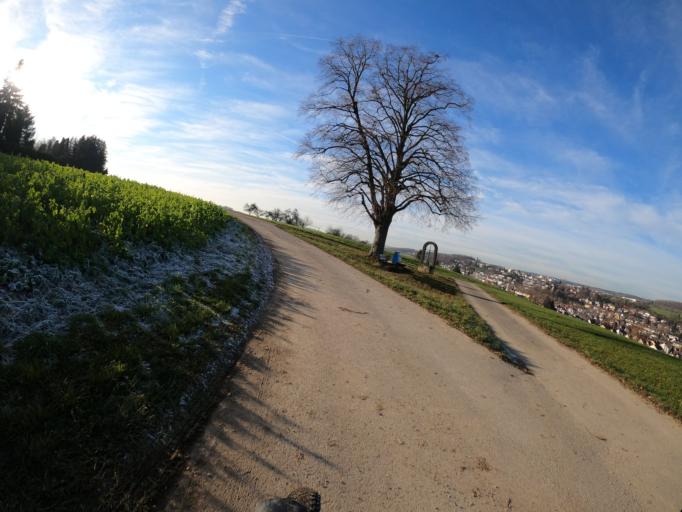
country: DE
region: Baden-Wuerttemberg
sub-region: Regierungsbezirk Stuttgart
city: Wangen
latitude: 48.7060
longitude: 9.6245
